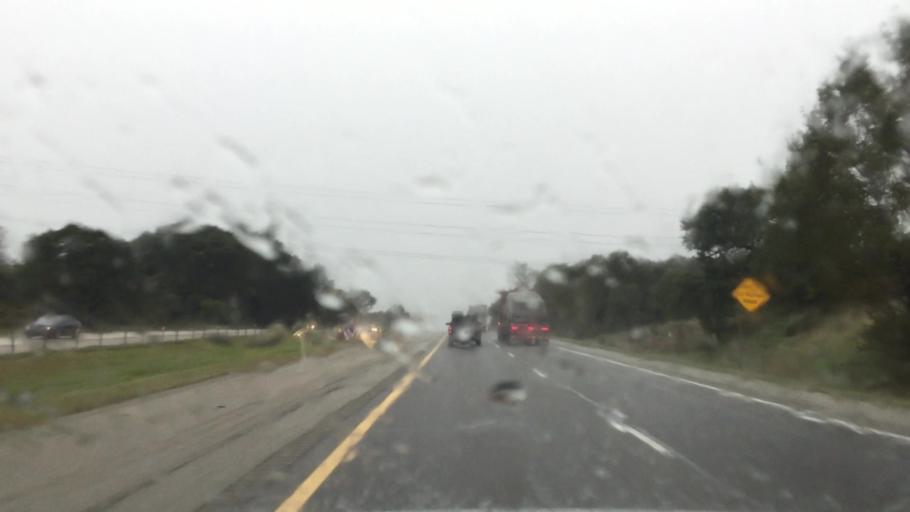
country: US
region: Michigan
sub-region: Van Buren County
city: Mattawan
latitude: 42.2232
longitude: -85.7631
